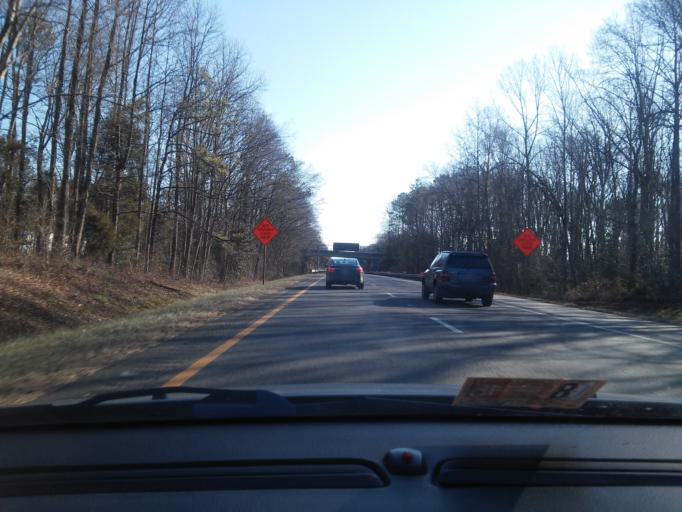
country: US
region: Virginia
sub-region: Henrico County
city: Wyndham
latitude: 37.6886
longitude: -77.6866
